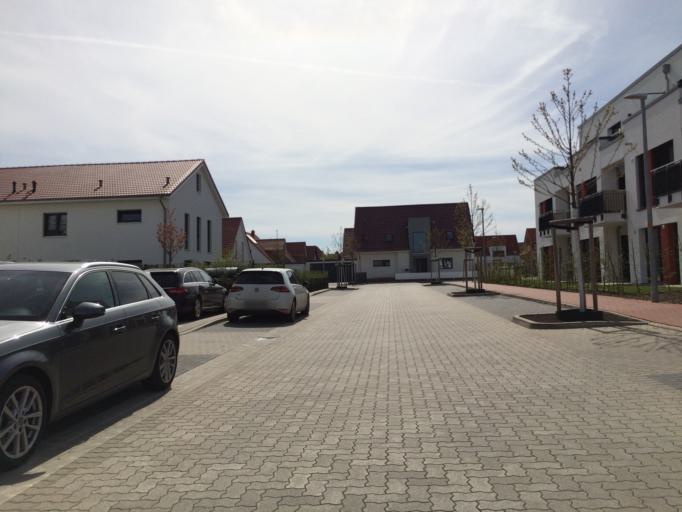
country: DE
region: Lower Saxony
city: Gehrden
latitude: 52.3118
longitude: 9.6151
